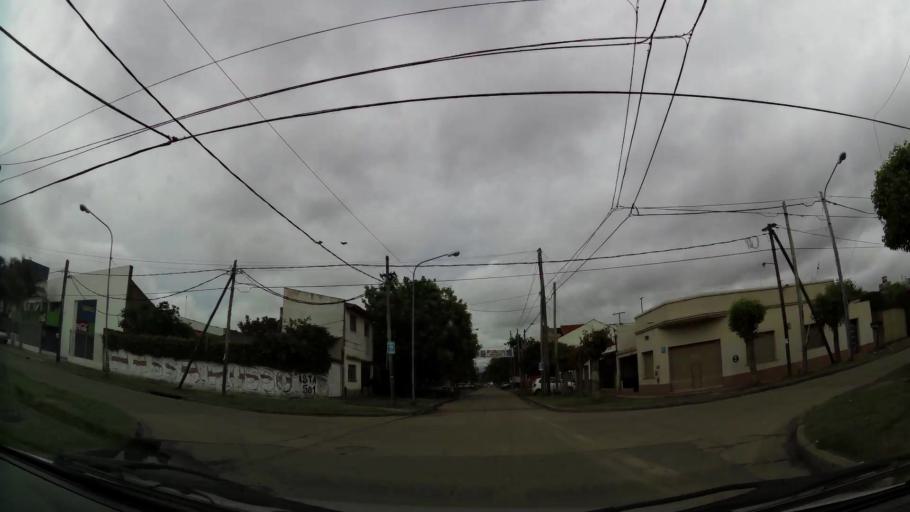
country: AR
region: Buenos Aires
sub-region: Partido de Lanus
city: Lanus
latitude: -34.7261
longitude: -58.3746
